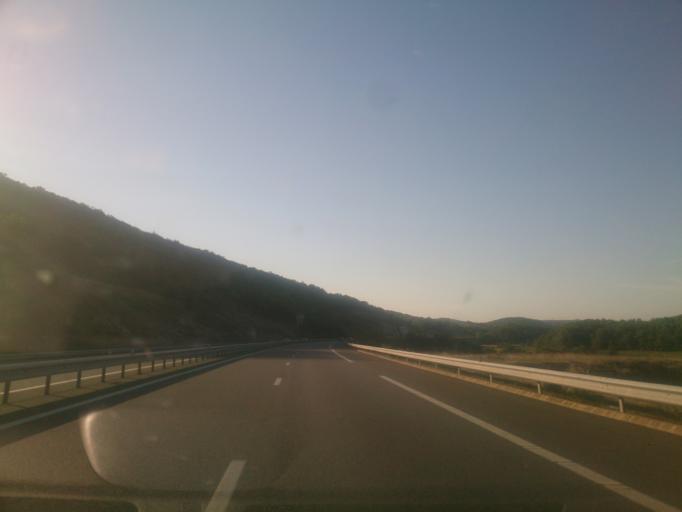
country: FR
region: Midi-Pyrenees
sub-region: Departement du Lot
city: Le Vigan
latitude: 44.7966
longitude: 1.5134
